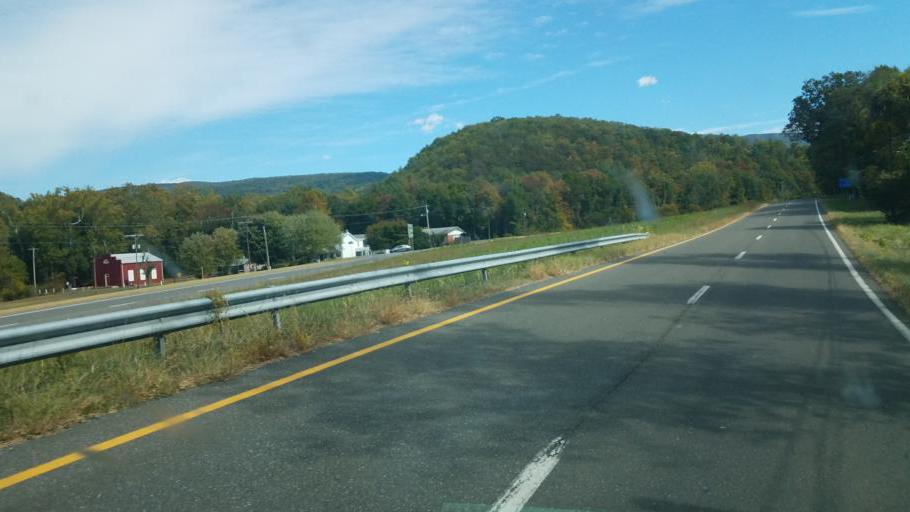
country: US
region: Virginia
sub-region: Page County
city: Luray
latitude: 38.6730
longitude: -78.3851
